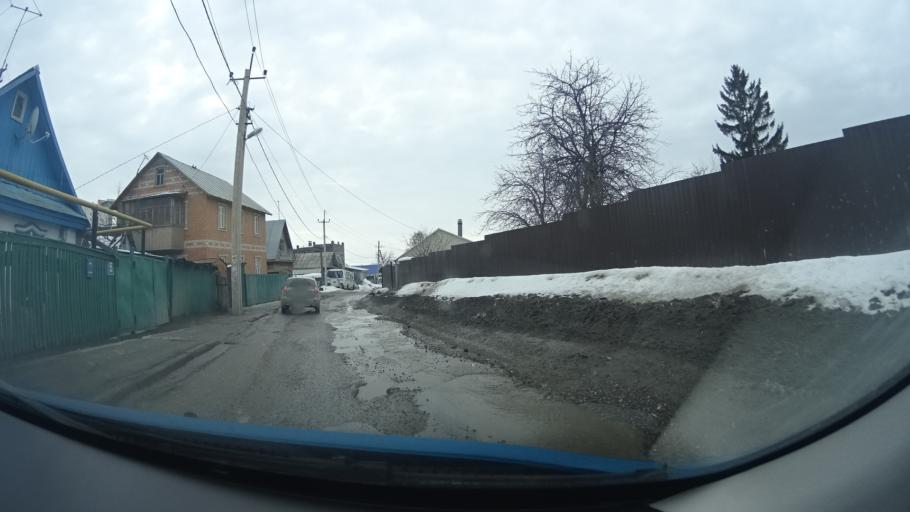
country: RU
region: Bashkortostan
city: Ufa
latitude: 54.6921
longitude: 55.9885
